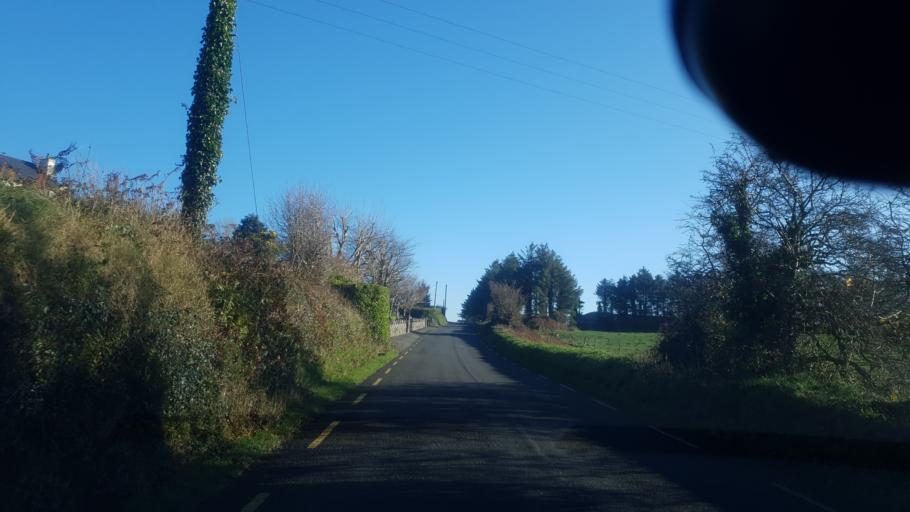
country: IE
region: Munster
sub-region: Ciarrai
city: Cill Airne
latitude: 52.1080
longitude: -9.4898
